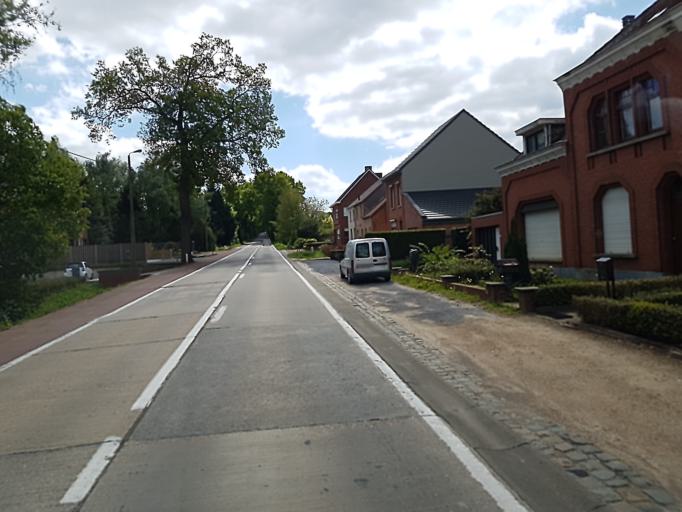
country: BE
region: Flanders
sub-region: Provincie Vlaams-Brabant
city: Diest
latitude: 51.0046
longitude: 5.0279
